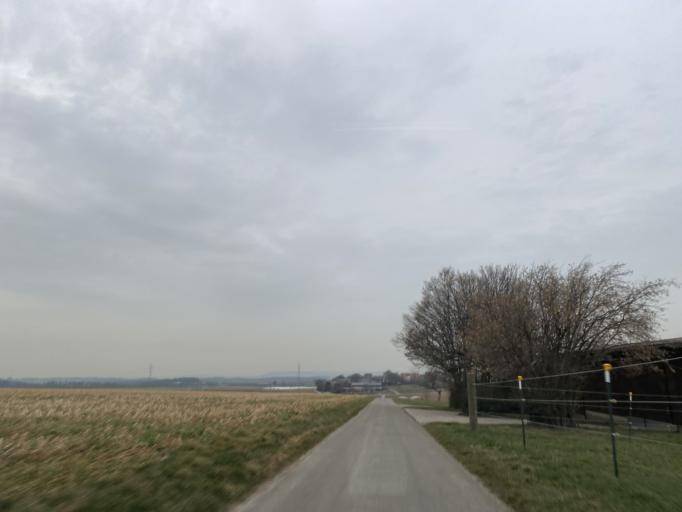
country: DE
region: Baden-Wuerttemberg
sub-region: Regierungsbezirk Stuttgart
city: Eberdingen
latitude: 48.8859
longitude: 8.9352
